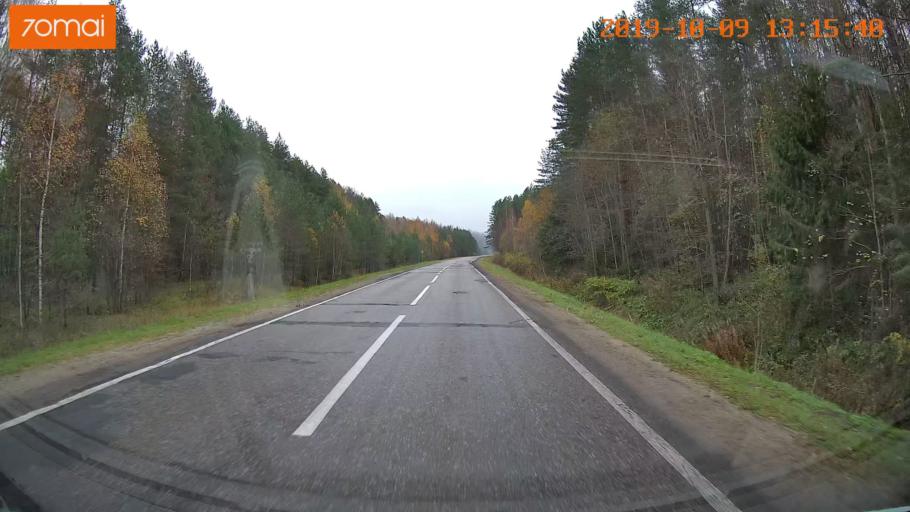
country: RU
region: Jaroslavl
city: Lyubim
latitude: 58.3662
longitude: 40.7555
